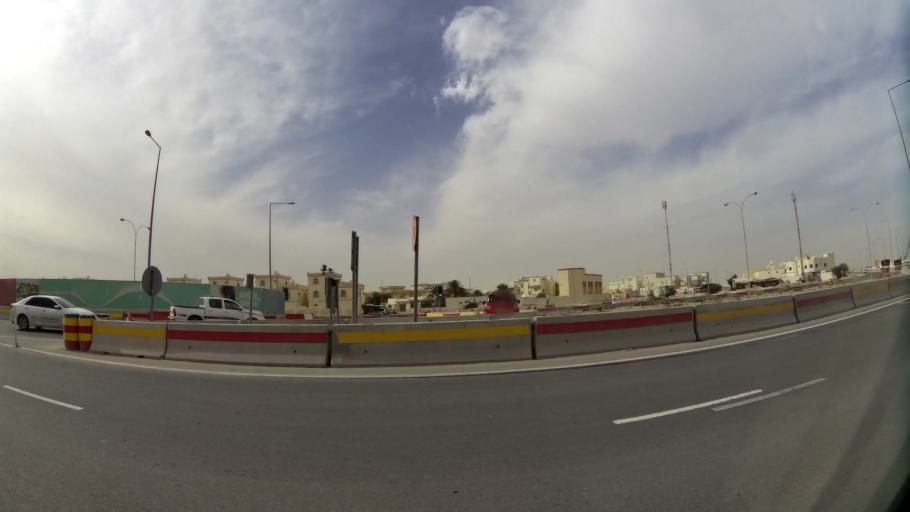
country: QA
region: Baladiyat ar Rayyan
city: Ar Rayyan
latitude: 25.3118
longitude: 51.4151
